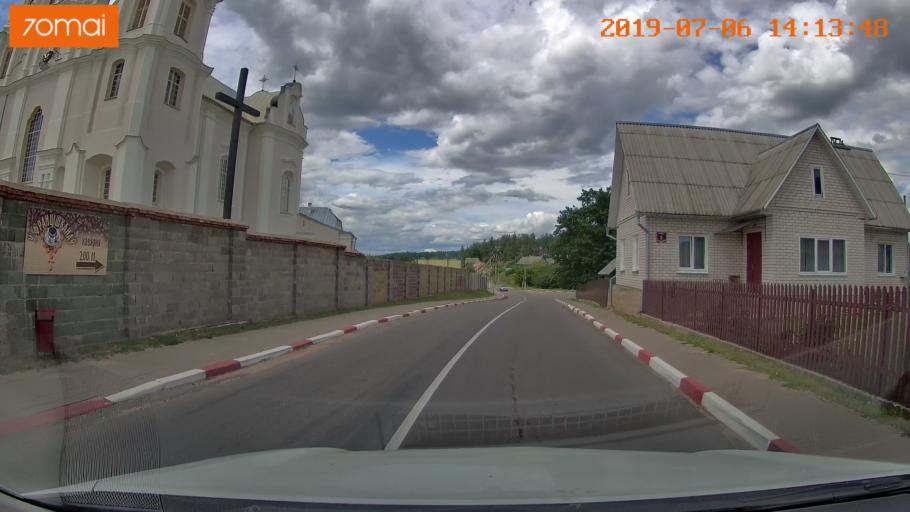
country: BY
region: Minsk
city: Ivyanyets
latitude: 53.8909
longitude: 26.7380
